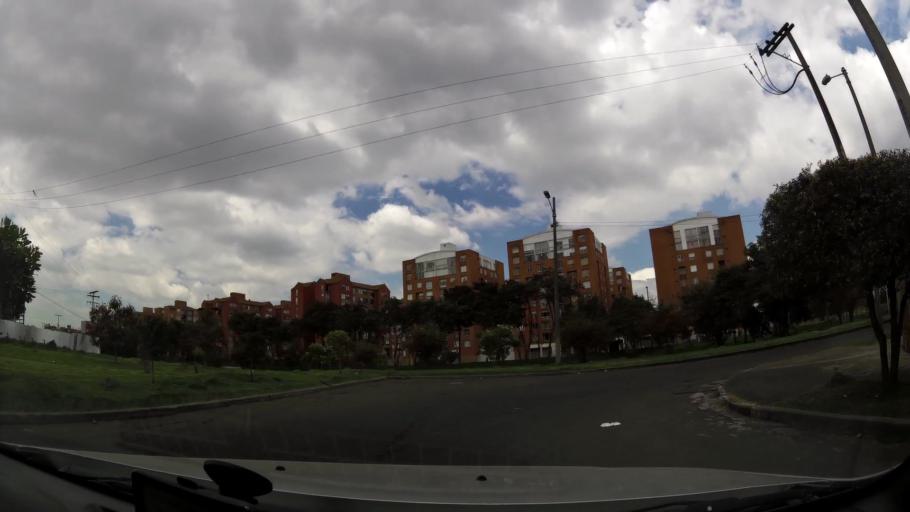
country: CO
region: Bogota D.C.
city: Bogota
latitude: 4.6391
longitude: -74.1021
